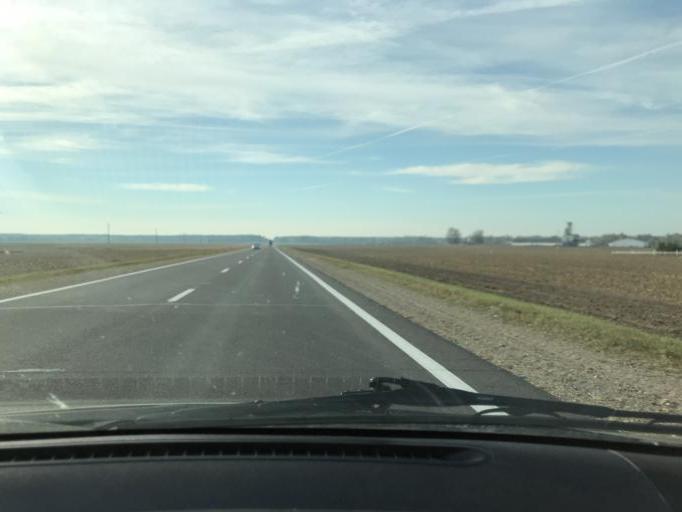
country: BY
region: Brest
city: Horad Pinsk
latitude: 52.1489
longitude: 25.8808
